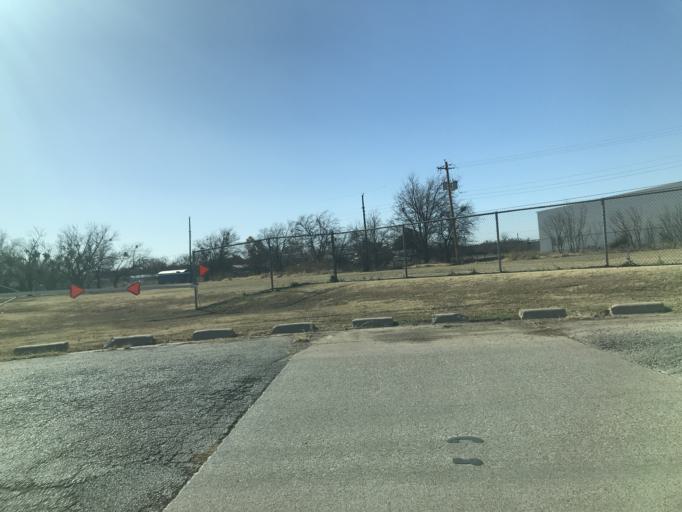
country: US
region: Texas
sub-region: Taylor County
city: Abilene
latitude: 32.4425
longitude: -99.7099
